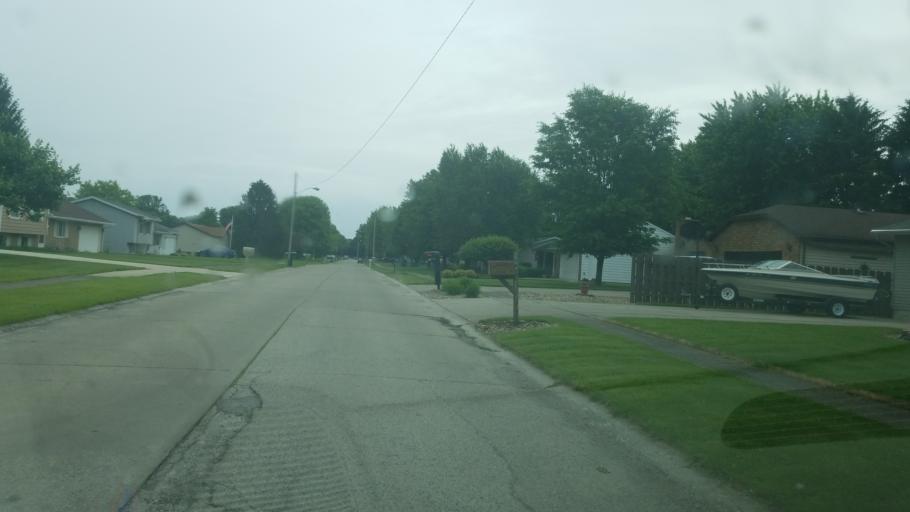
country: US
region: Ohio
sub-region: Crawford County
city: Bucyrus
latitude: 40.7907
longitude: -82.9879
